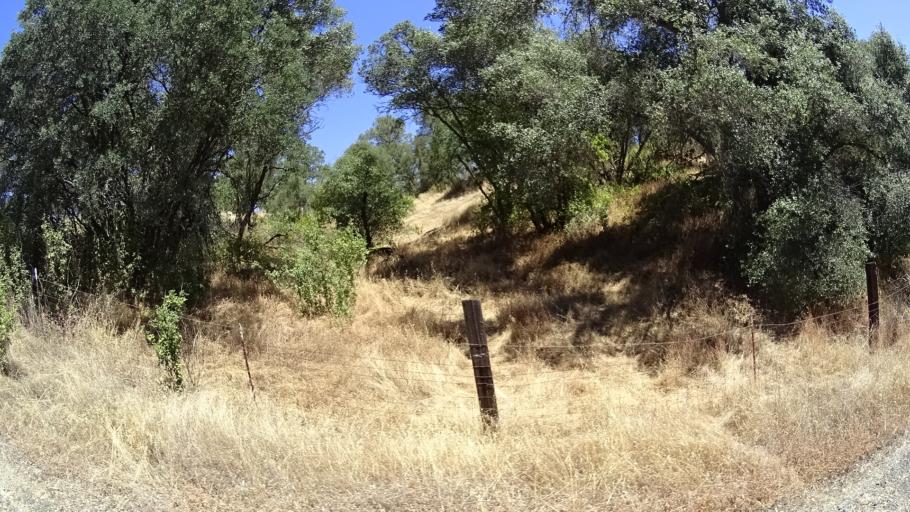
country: US
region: California
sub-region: Calaveras County
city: Copperopolis
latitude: 37.9654
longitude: -120.6974
